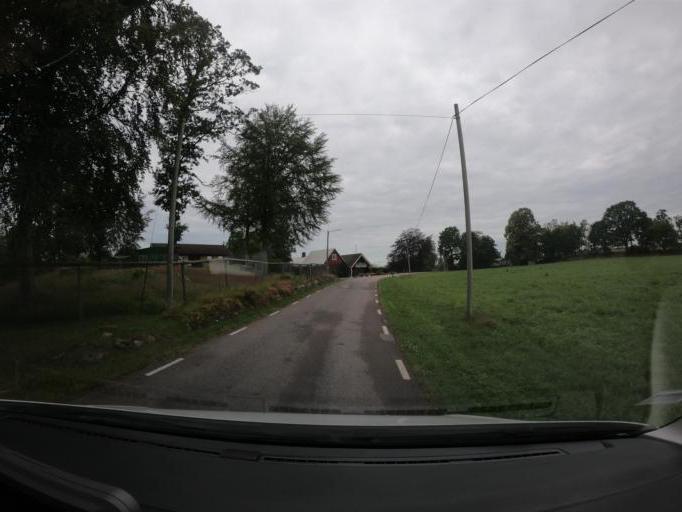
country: SE
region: Skane
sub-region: Klippans Kommun
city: Klippan
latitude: 56.2697
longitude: 13.1341
